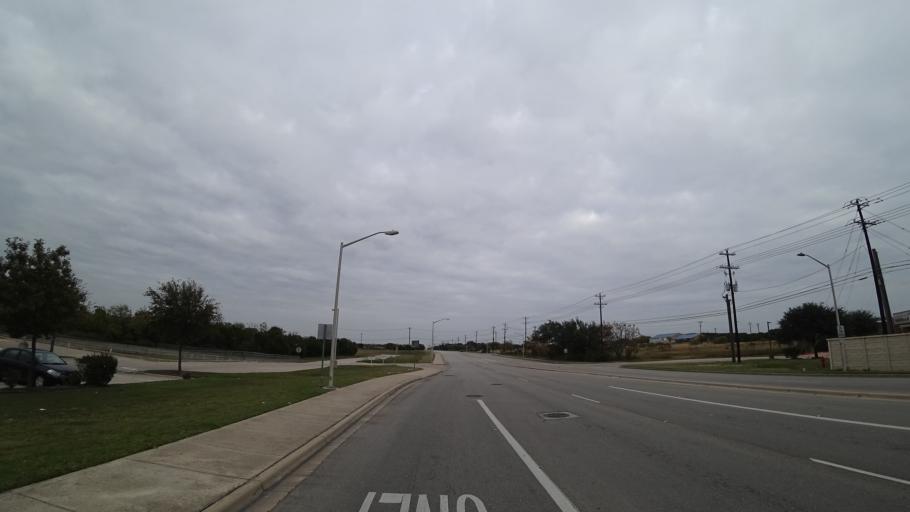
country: US
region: Texas
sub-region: Williamson County
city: Cedar Park
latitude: 30.5301
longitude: -97.8446
